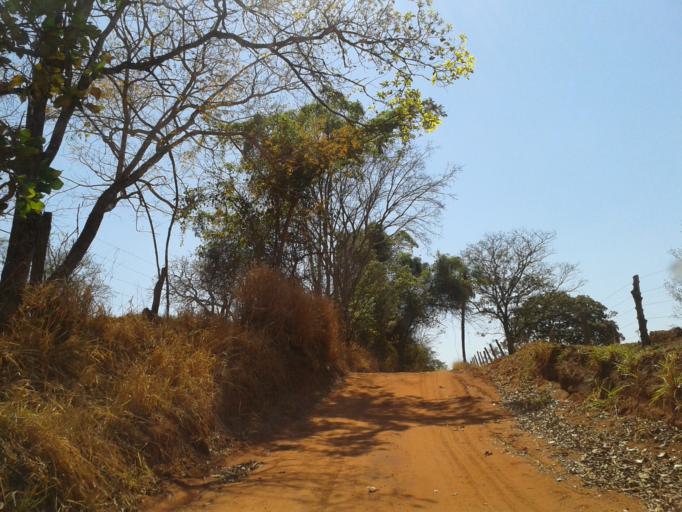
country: BR
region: Minas Gerais
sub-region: Ituiutaba
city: Ituiutaba
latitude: -19.0848
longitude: -49.3023
